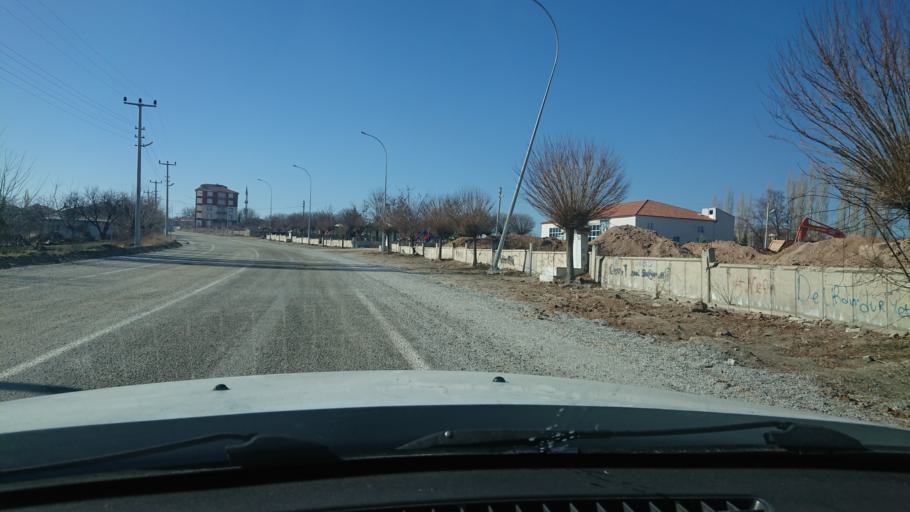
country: TR
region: Aksaray
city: Agacoren
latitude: 38.8718
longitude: 33.9103
